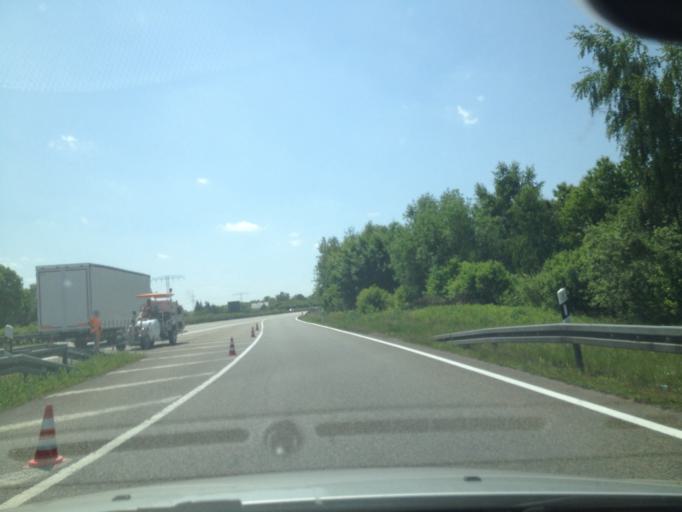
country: DE
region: Saxony
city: Neukirchen
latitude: 50.8041
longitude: 12.8579
